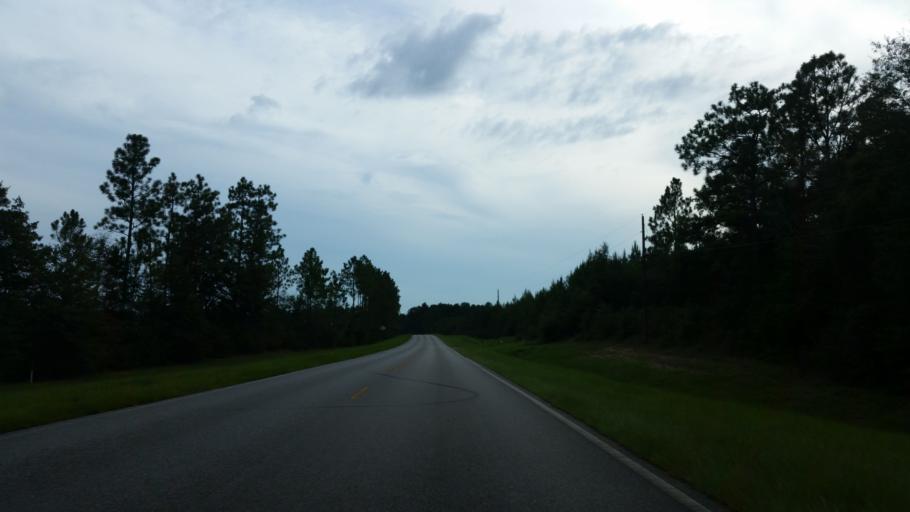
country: US
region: Florida
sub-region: Santa Rosa County
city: Point Baker
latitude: 30.7067
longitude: -86.9744
